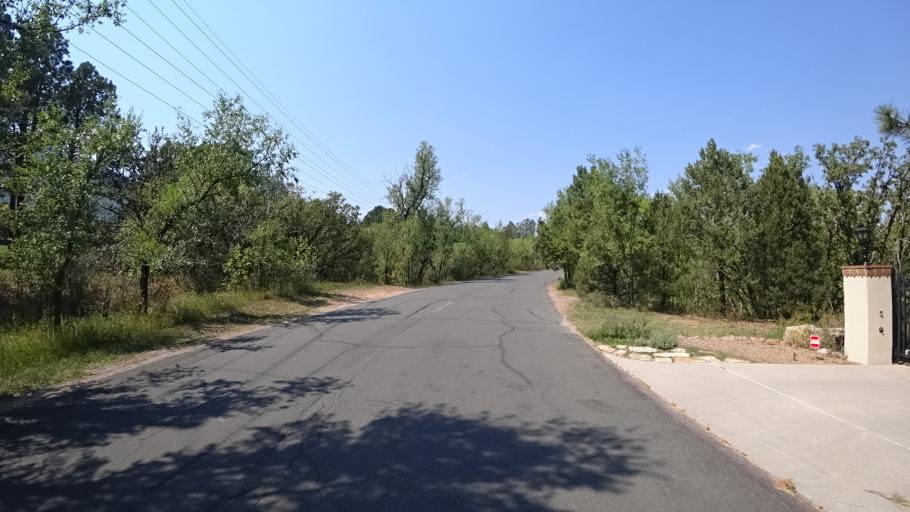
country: US
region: Colorado
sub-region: El Paso County
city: Colorado Springs
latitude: 38.7814
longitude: -104.8434
